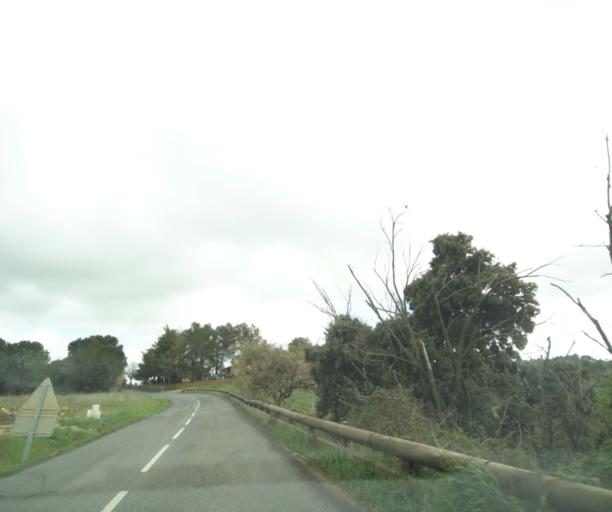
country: FR
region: Languedoc-Roussillon
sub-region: Departement de l'Herault
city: Murviel-les-Montpellier
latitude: 43.5968
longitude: 3.7454
